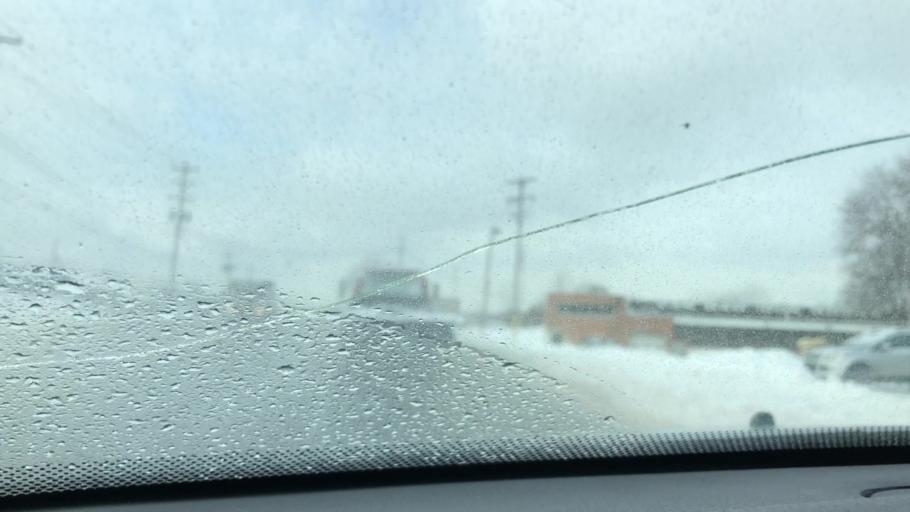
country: US
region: Michigan
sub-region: Kent County
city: Wyoming
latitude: 42.9354
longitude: -85.7102
